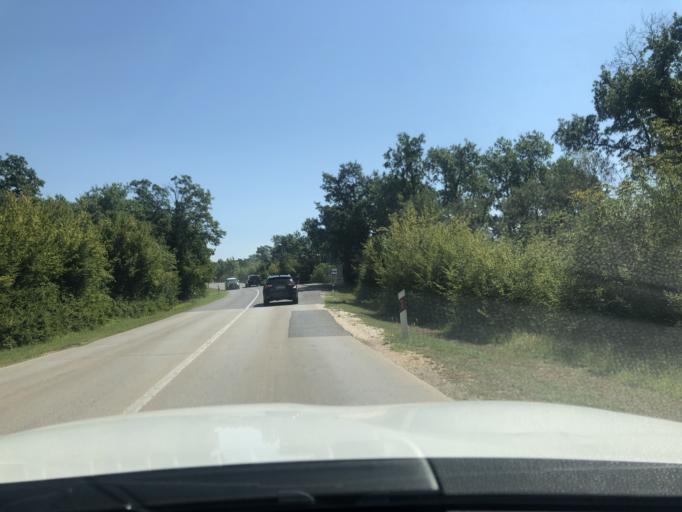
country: HR
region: Istarska
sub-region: Grad Rovinj
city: Rovinj
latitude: 45.0504
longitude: 13.7261
